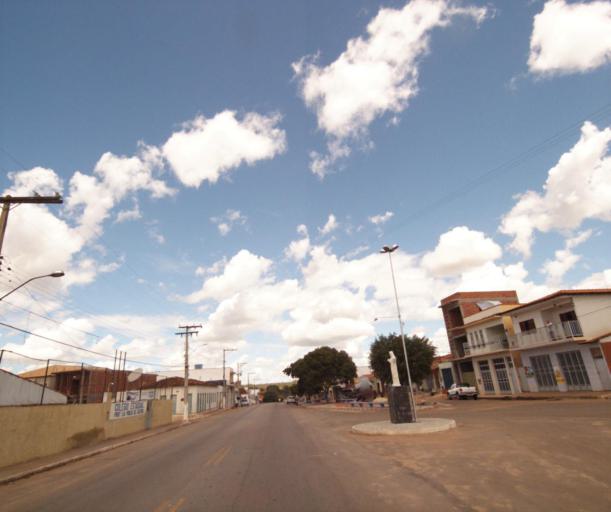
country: BR
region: Bahia
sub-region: Cacule
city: Cacule
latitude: -14.2060
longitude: -42.1117
